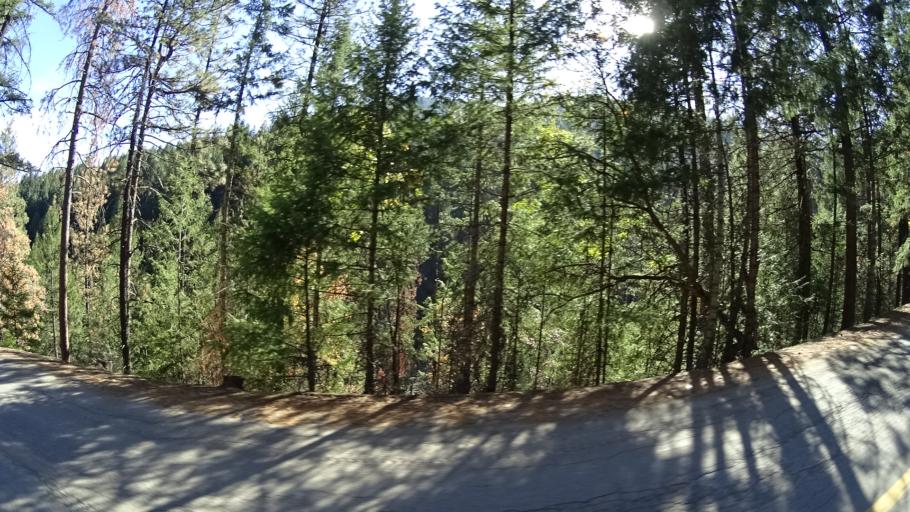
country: US
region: California
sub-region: Siskiyou County
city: Yreka
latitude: 41.7284
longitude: -122.7133
